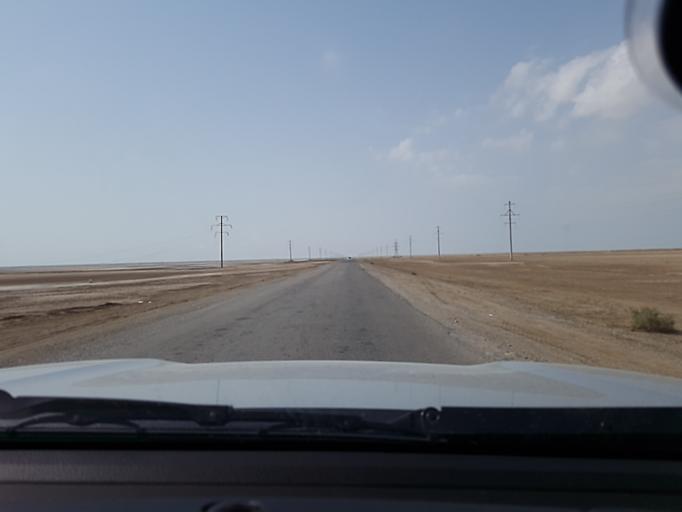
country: TM
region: Balkan
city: Gumdag
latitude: 39.0874
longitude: 54.5844
